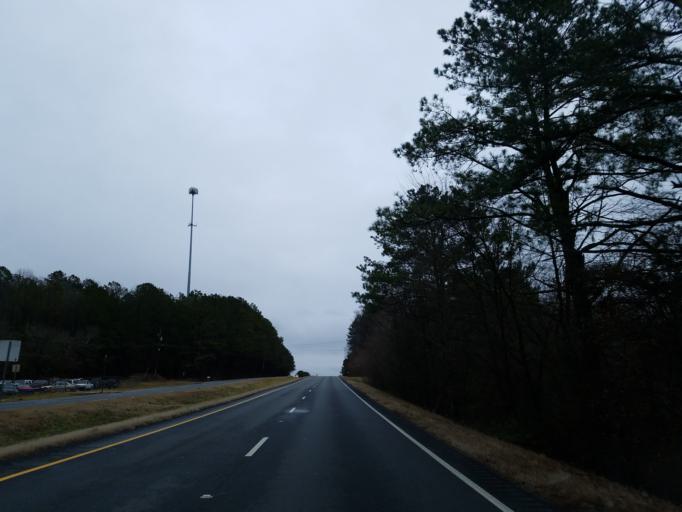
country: US
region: Georgia
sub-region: Bartow County
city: Cartersville
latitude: 34.2170
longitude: -84.8393
